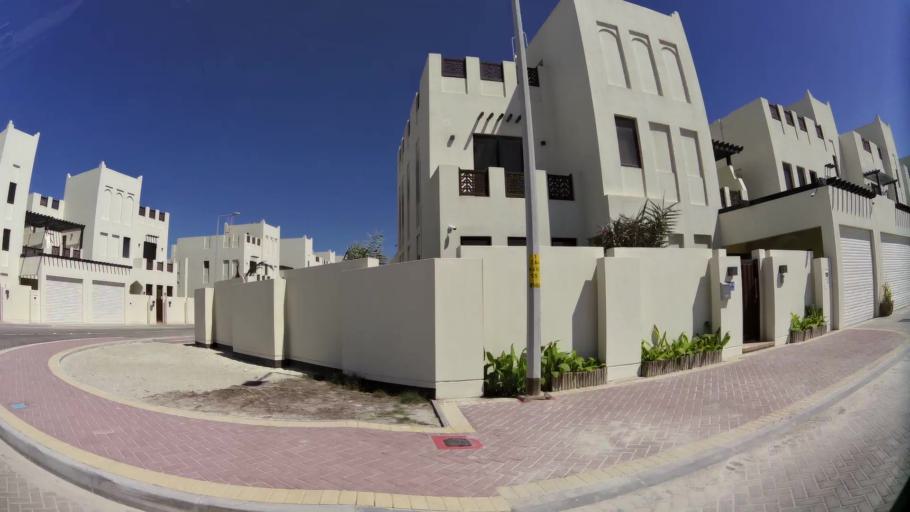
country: BH
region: Muharraq
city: Al Muharraq
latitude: 26.3025
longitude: 50.6356
